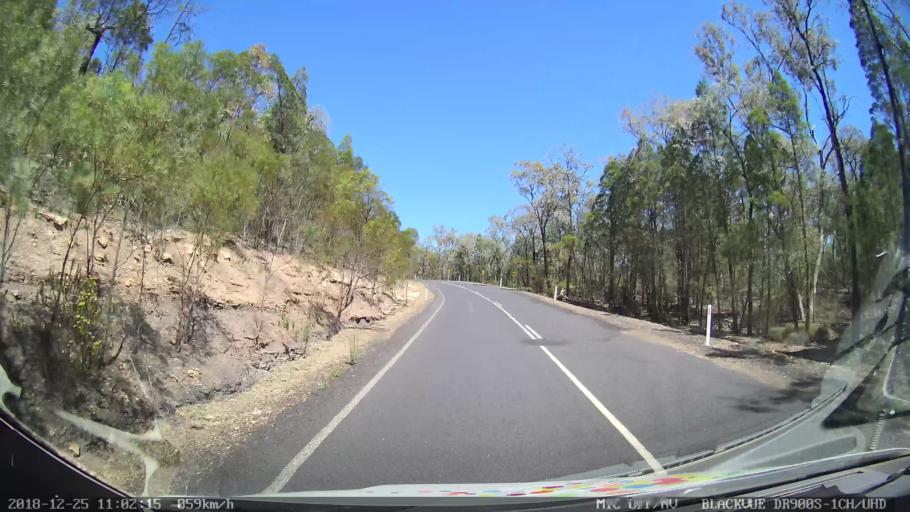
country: AU
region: New South Wales
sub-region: Upper Hunter Shire
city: Merriwa
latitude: -32.4048
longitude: 150.1924
